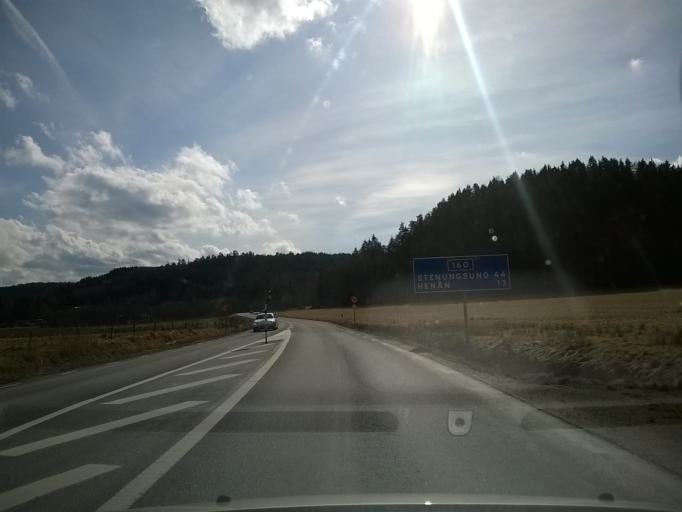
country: SE
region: Vaestra Goetaland
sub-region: Orust
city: Henan
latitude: 58.3401
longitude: 11.6915
